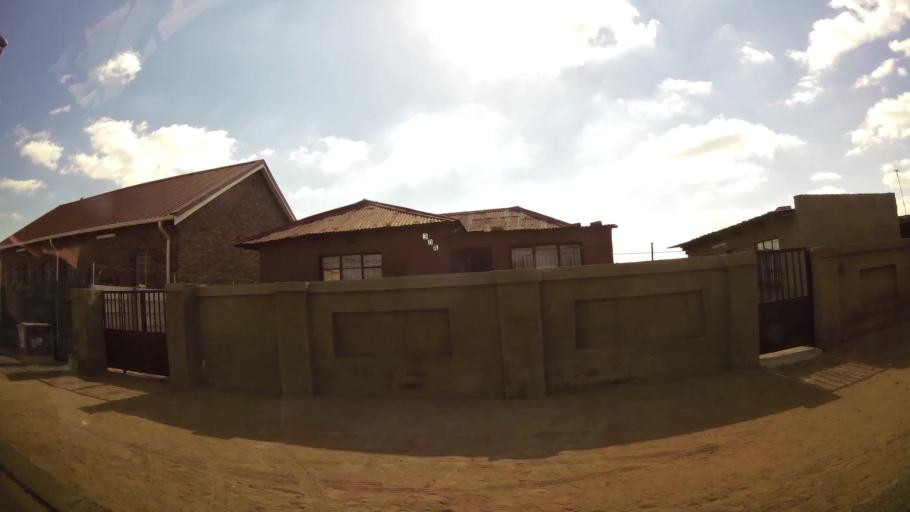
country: ZA
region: Gauteng
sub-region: West Rand District Municipality
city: Krugersdorp
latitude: -26.1402
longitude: 27.7958
